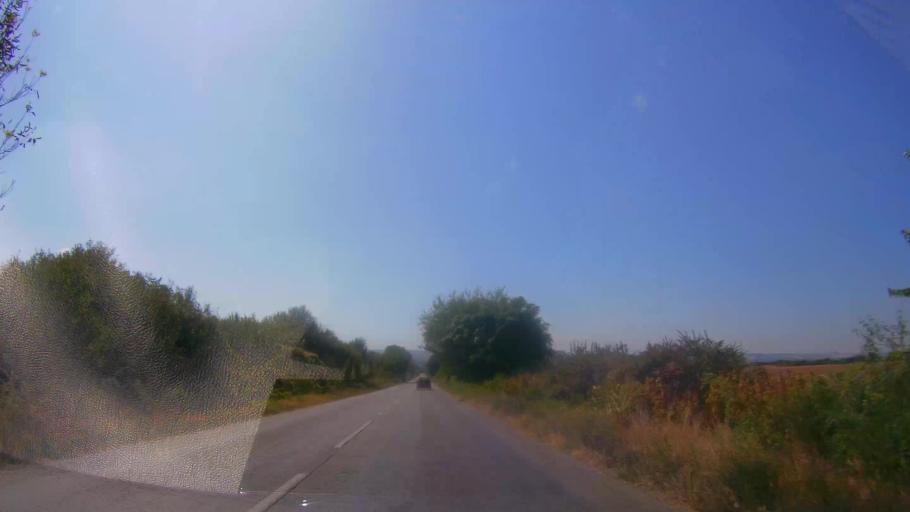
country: BG
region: Veliko Turnovo
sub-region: Obshtina Gorna Oryakhovitsa
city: Purvomaytsi
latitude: 43.2289
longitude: 25.6395
